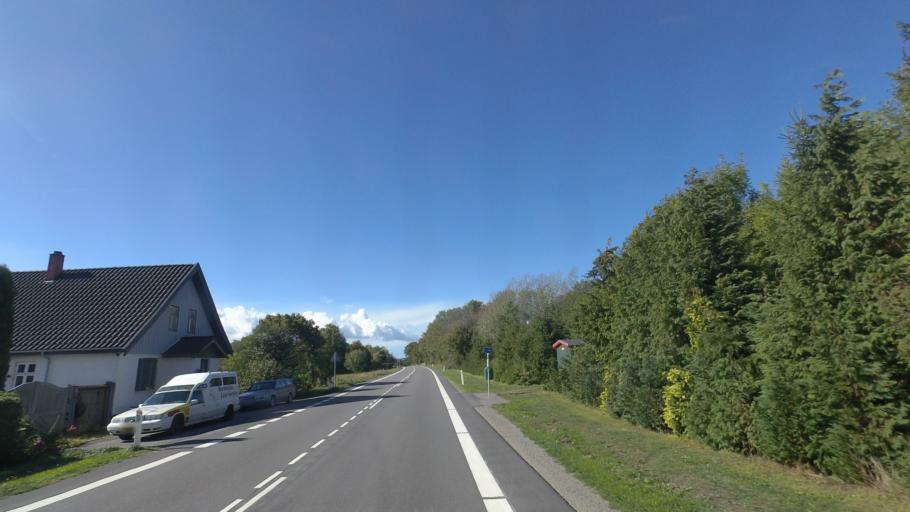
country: DK
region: Capital Region
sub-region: Bornholm Kommune
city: Akirkeby
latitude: 55.0678
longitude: 14.9968
